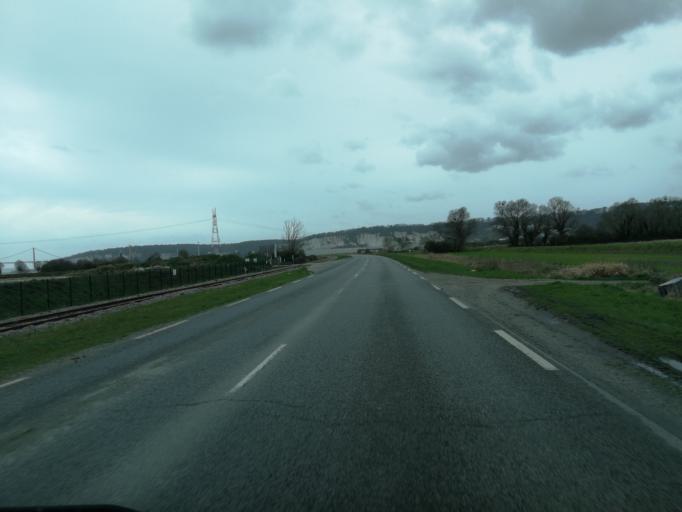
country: FR
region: Haute-Normandie
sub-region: Departement de l'Eure
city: Quillebeuf-sur-Seine
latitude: 49.4895
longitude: 0.5029
